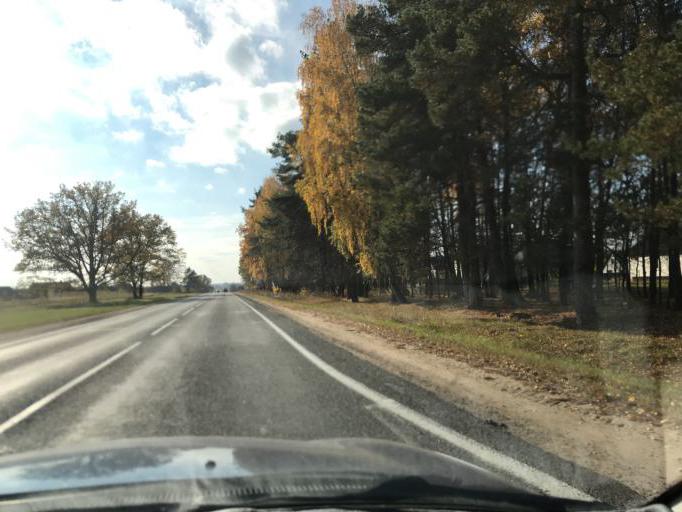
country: BY
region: Grodnenskaya
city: Voranava
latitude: 54.1645
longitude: 25.3291
